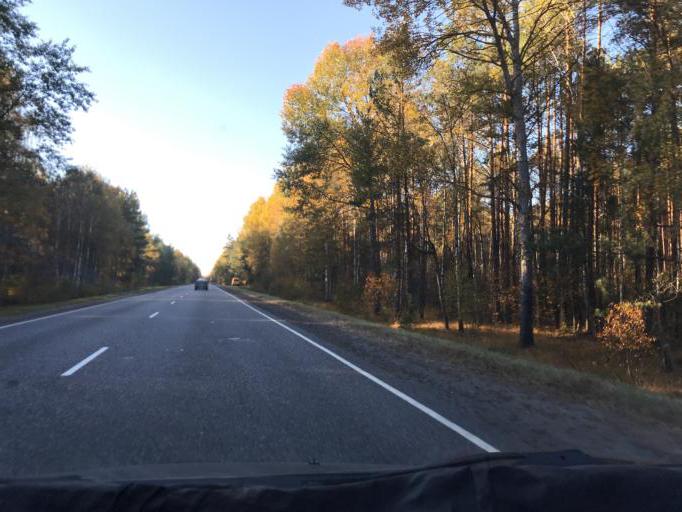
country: BY
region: Gomel
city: Pyetrykaw
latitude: 52.2489
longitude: 28.3710
